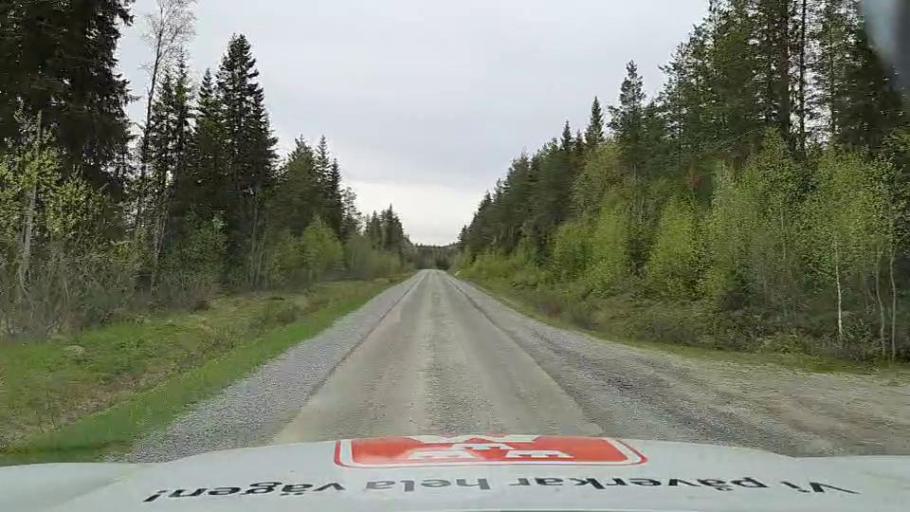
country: SE
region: Jaemtland
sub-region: OEstersunds Kommun
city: Brunflo
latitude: 62.6415
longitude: 14.9327
